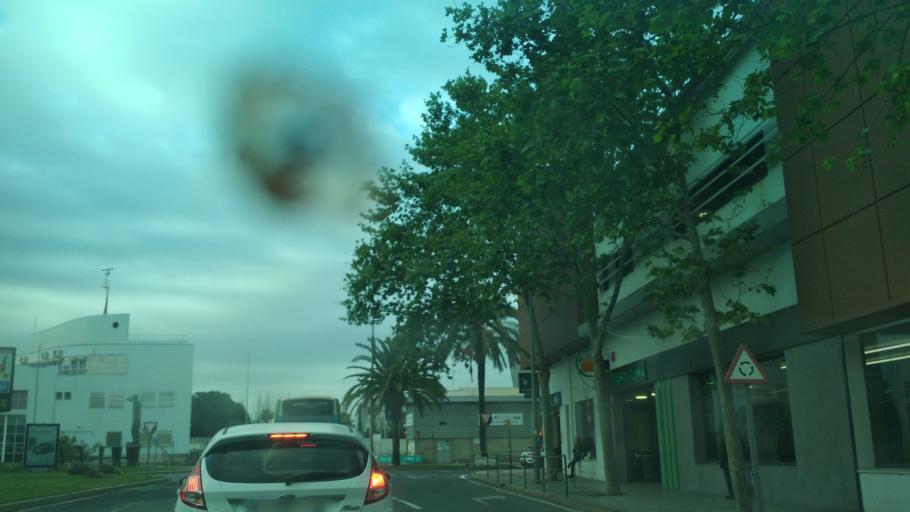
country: ES
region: Andalusia
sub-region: Provincia de Huelva
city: Huelva
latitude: 37.2627
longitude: -6.9593
